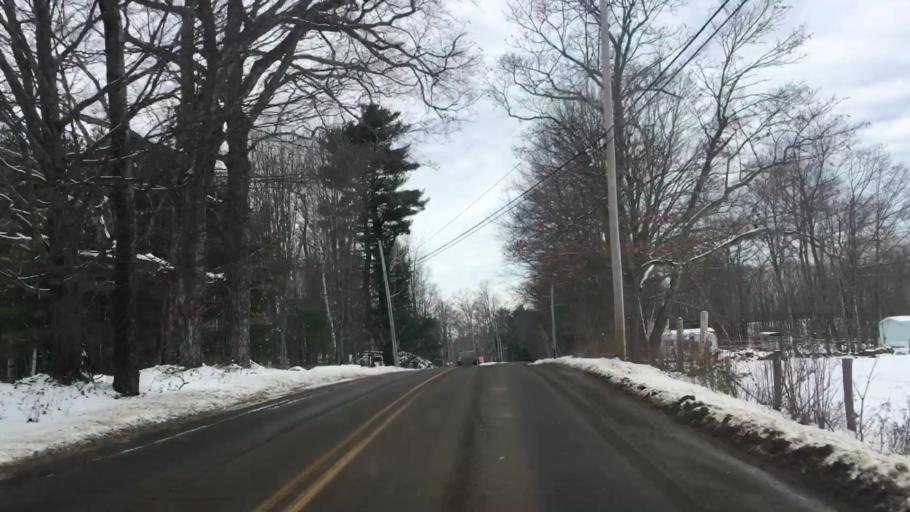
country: US
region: Maine
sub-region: Kennebec County
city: Chelsea
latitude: 44.2566
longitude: -69.6425
